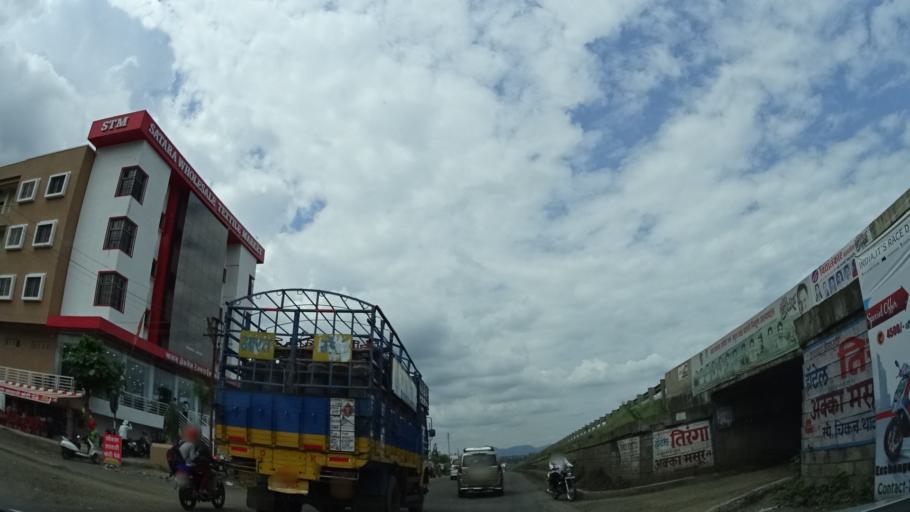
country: IN
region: Maharashtra
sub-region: Satara Division
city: Satara
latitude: 17.7018
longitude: 74.0256
